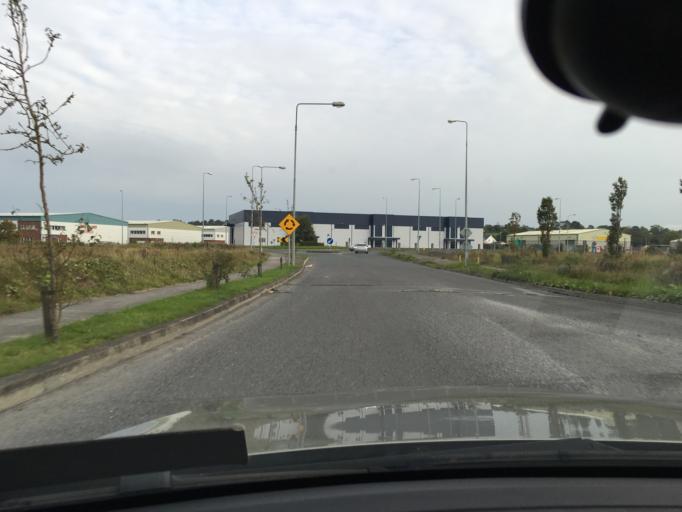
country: IE
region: Leinster
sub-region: An Longfort
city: Longford
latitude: 53.7215
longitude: -7.8118
